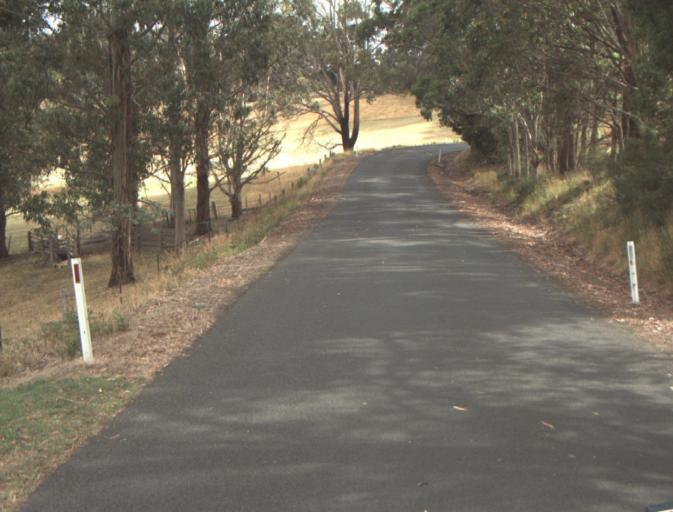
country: AU
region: Tasmania
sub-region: Dorset
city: Scottsdale
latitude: -41.4583
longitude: 147.5959
